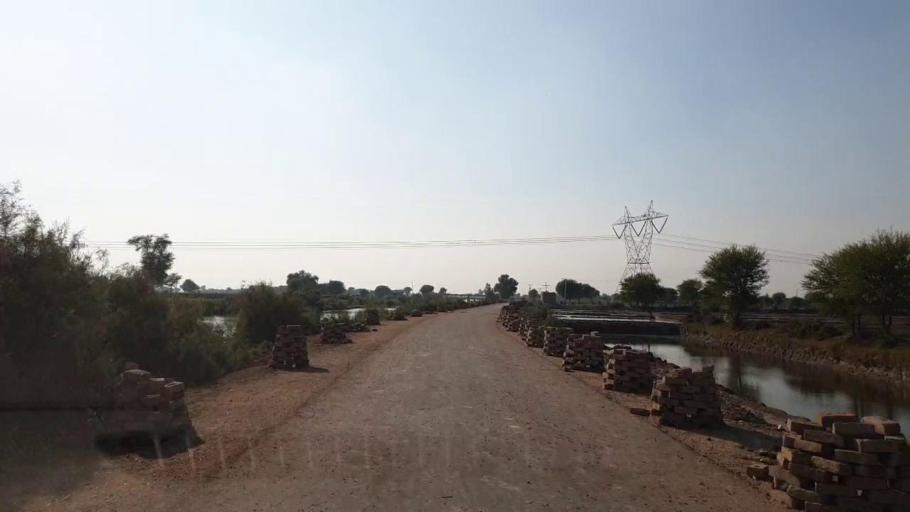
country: PK
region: Sindh
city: Sehwan
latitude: 26.4384
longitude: 67.8019
